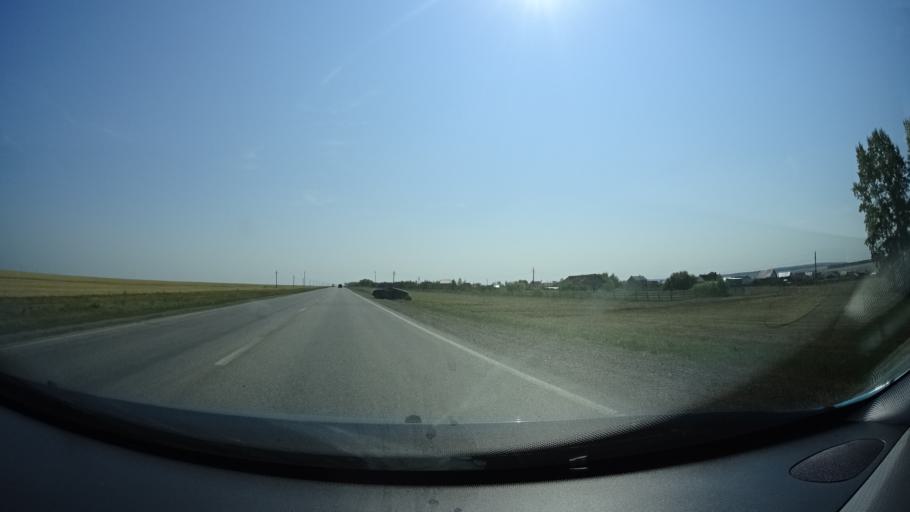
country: RU
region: Bashkortostan
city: Kabakovo
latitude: 54.4300
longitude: 56.0223
